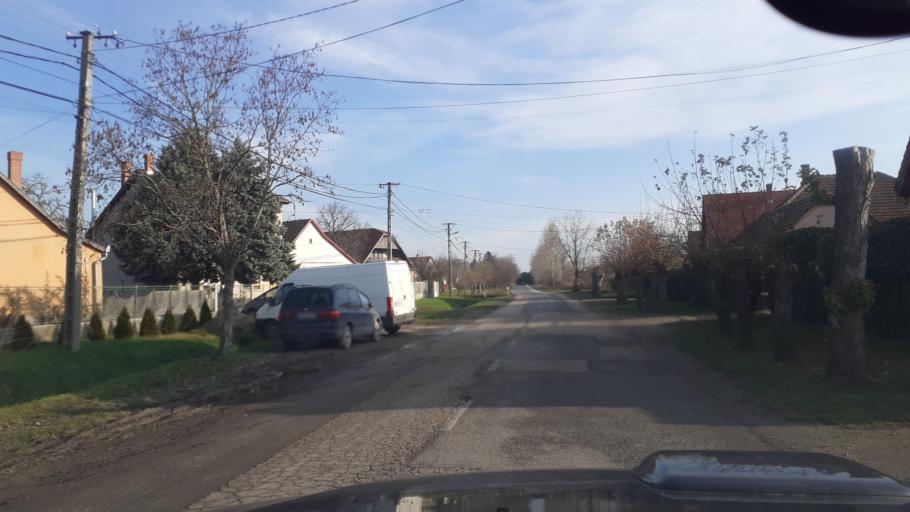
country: HU
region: Pest
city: Domsod
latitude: 47.0912
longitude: 19.0249
